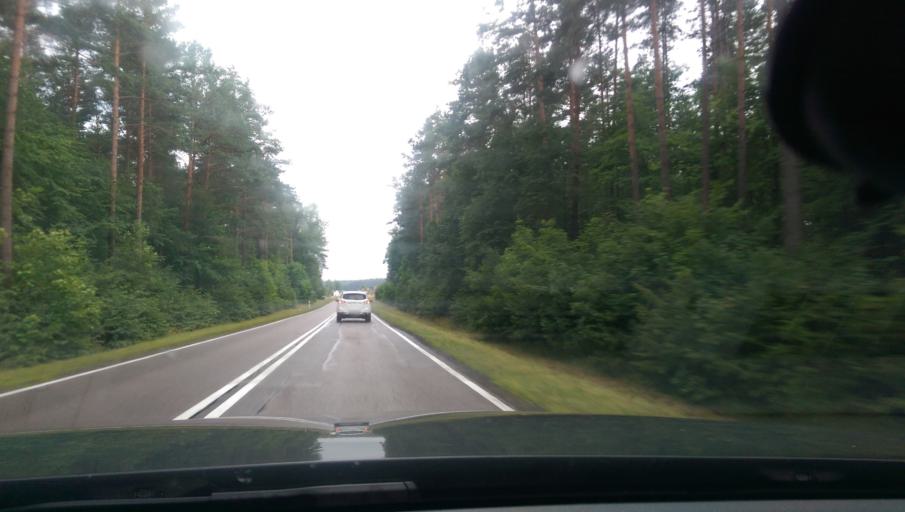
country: PL
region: Warmian-Masurian Voivodeship
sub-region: Powiat szczycienski
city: Szczytno
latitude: 53.5070
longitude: 20.9693
